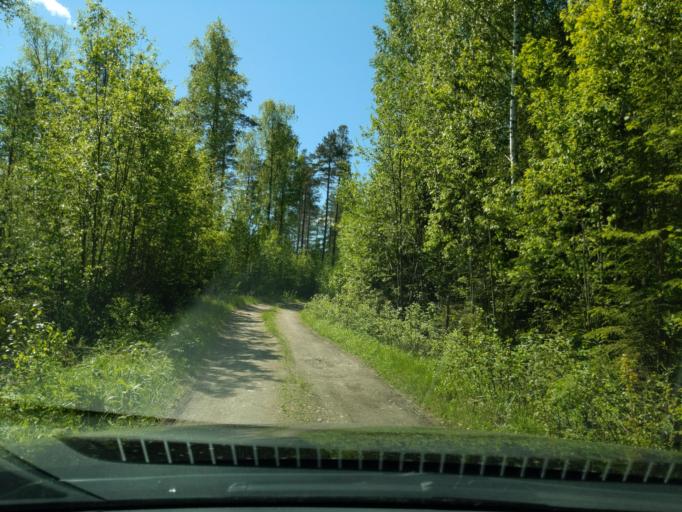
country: FI
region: Paijanne Tavastia
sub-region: Lahti
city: Lahti
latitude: 61.0499
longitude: 25.6966
